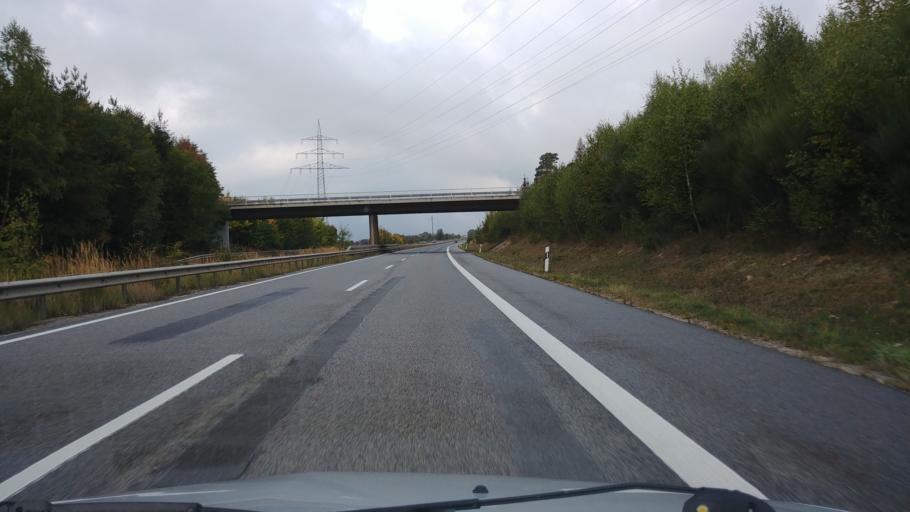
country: DE
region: Rheinland-Pfalz
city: Niedersohren
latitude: 49.9359
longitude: 7.3416
